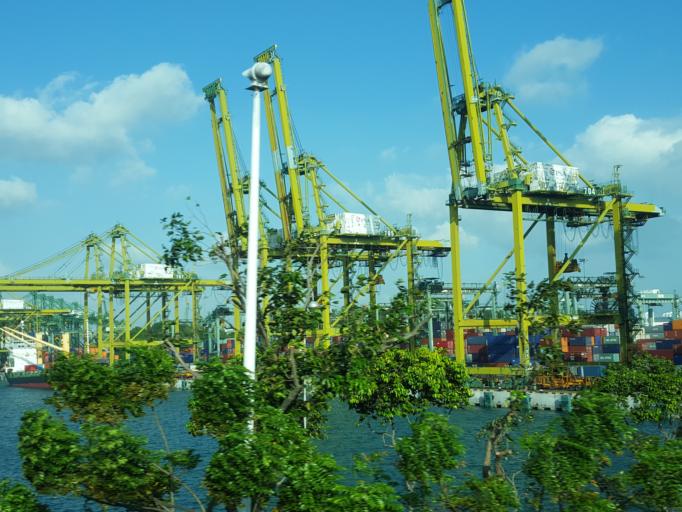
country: SG
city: Singapore
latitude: 1.2612
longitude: 103.8238
